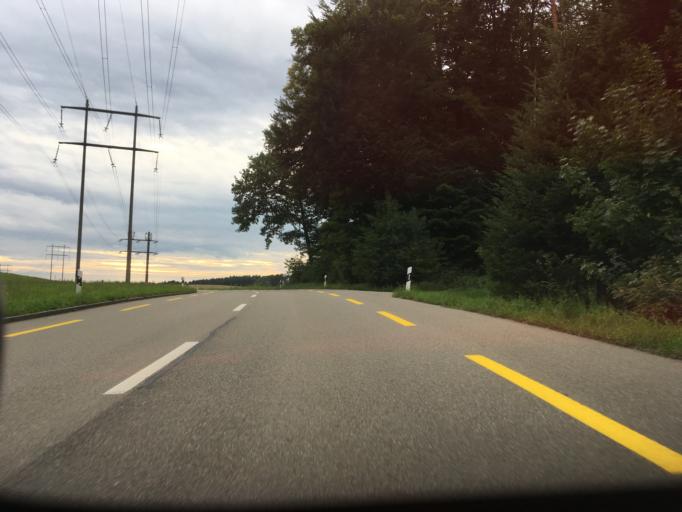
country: CH
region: Zurich
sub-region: Bezirk Uster
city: Gutenswil
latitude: 47.3887
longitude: 8.7275
